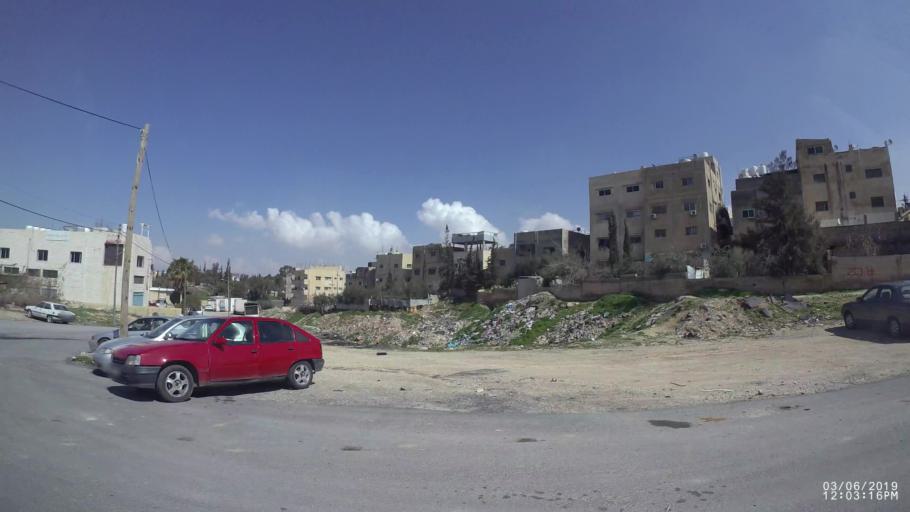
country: JO
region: Zarqa
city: Russeifa
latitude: 31.9894
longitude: 36.0154
